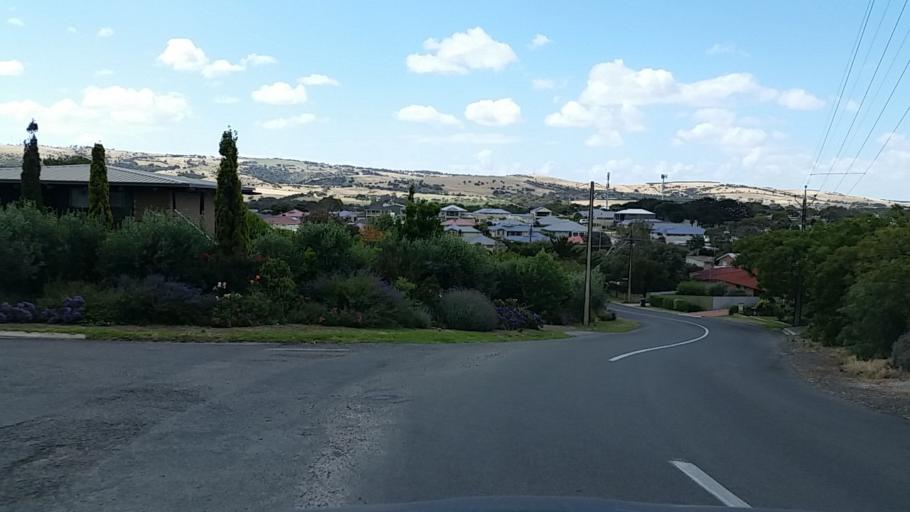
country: AU
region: South Australia
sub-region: Alexandrina
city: Port Elliot
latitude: -35.5330
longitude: 138.6736
